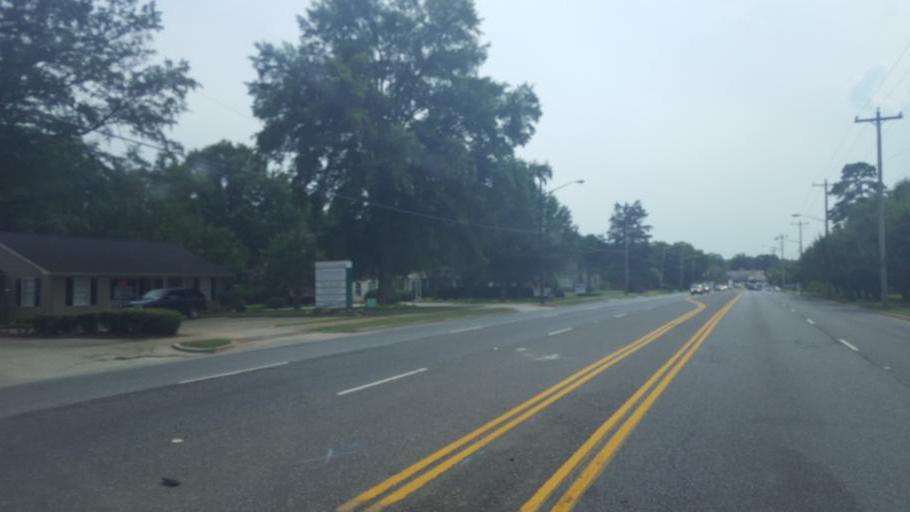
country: US
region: South Carolina
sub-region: York County
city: Rock Hill
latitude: 34.9471
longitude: -81.0238
